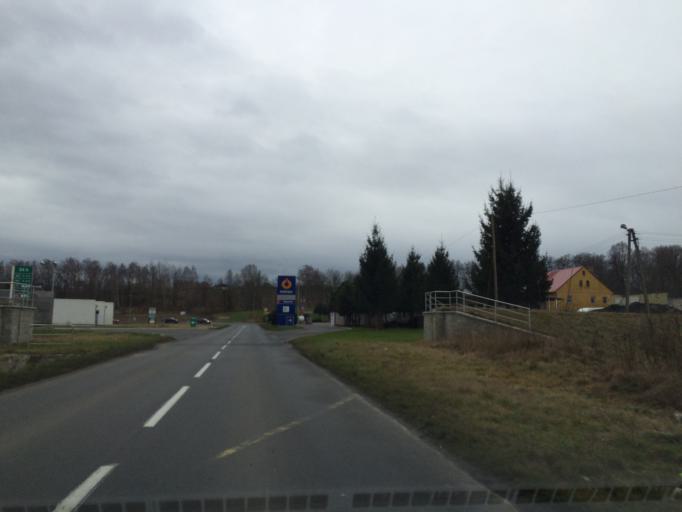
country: PL
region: Lower Silesian Voivodeship
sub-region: Powiat lwowecki
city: Lwowek Slaski
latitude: 51.1208
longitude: 15.5821
